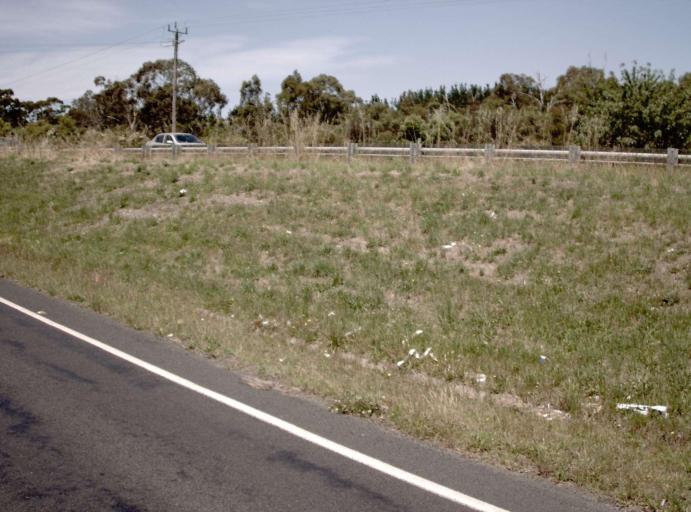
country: AU
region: Victoria
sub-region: Latrobe
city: Traralgon
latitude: -38.2077
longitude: 146.5001
